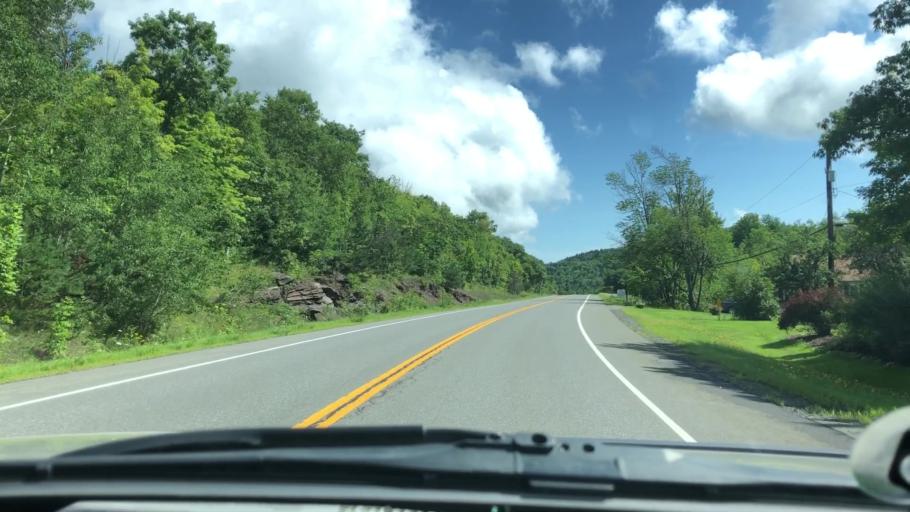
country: US
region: New York
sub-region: Greene County
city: Cairo
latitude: 42.3279
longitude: -74.1728
